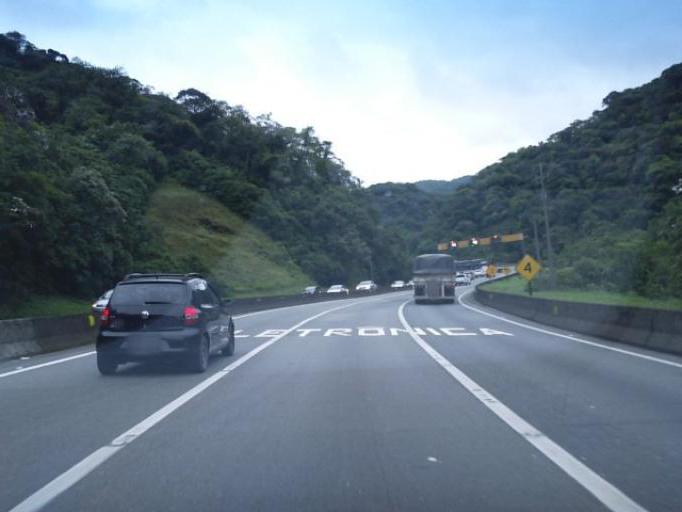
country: BR
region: Parana
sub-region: Guaratuba
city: Guaratuba
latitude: -25.8750
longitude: -48.9364
